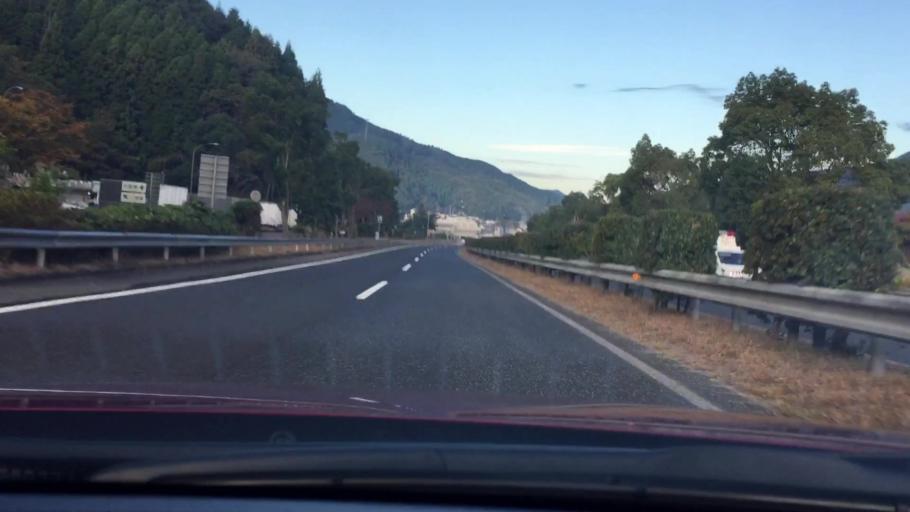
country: JP
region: Hyogo
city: Yamazakicho-nakabirose
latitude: 34.9843
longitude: 134.6047
